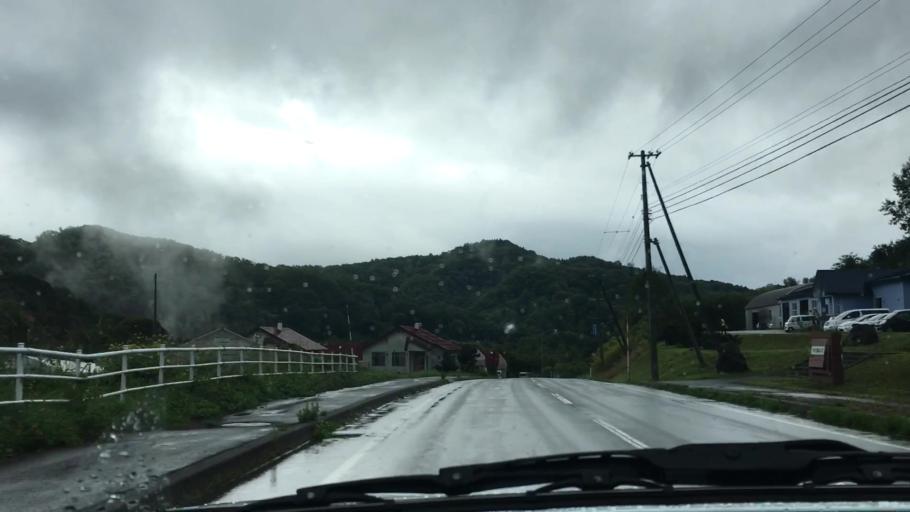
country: JP
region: Hokkaido
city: Niseko Town
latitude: 42.6418
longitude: 140.7330
